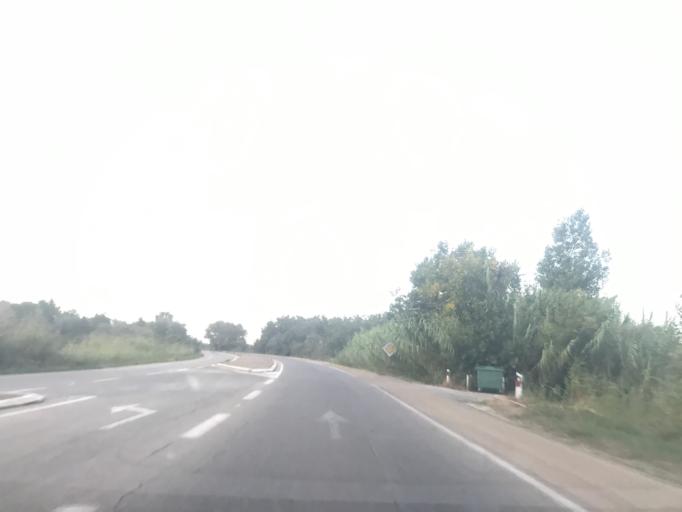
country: FR
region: Provence-Alpes-Cote d'Azur
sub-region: Departement des Bouches-du-Rhone
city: Saintes-Maries-de-la-Mer
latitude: 43.5264
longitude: 4.4009
